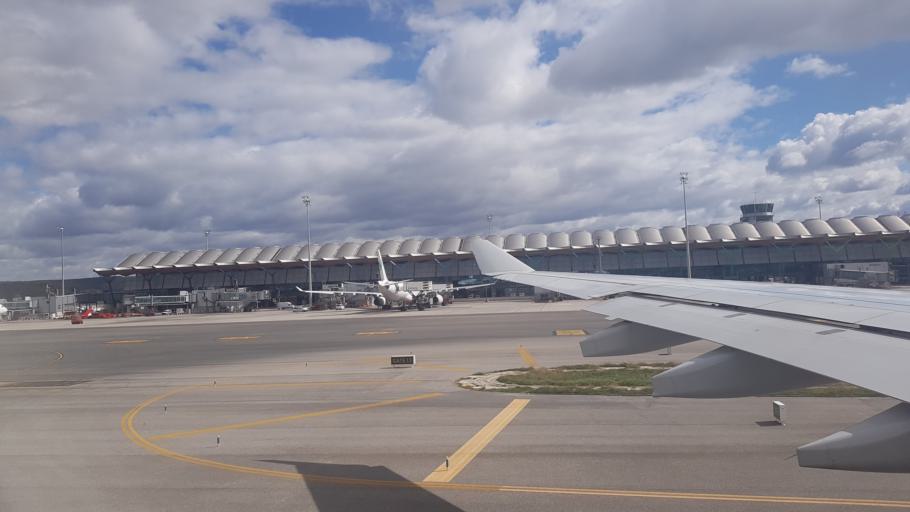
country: ES
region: Madrid
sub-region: Provincia de Madrid
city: Barajas de Madrid
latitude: 40.4970
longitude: -3.5712
